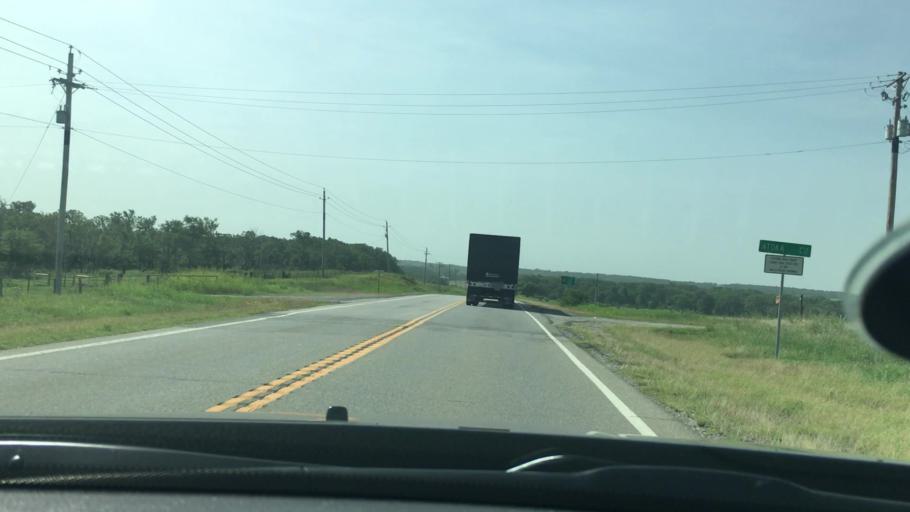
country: US
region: Oklahoma
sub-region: Atoka County
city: Atoka
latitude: 34.4189
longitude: -96.1889
